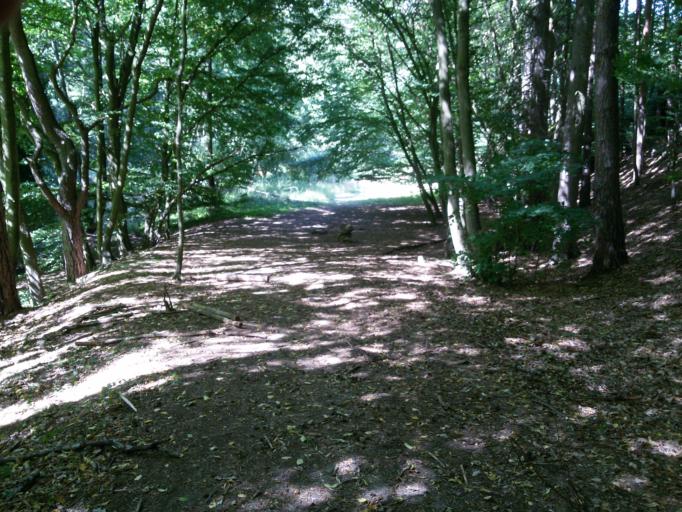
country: CZ
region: Vysocina
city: Rouchovany
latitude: 49.0367
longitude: 16.0689
